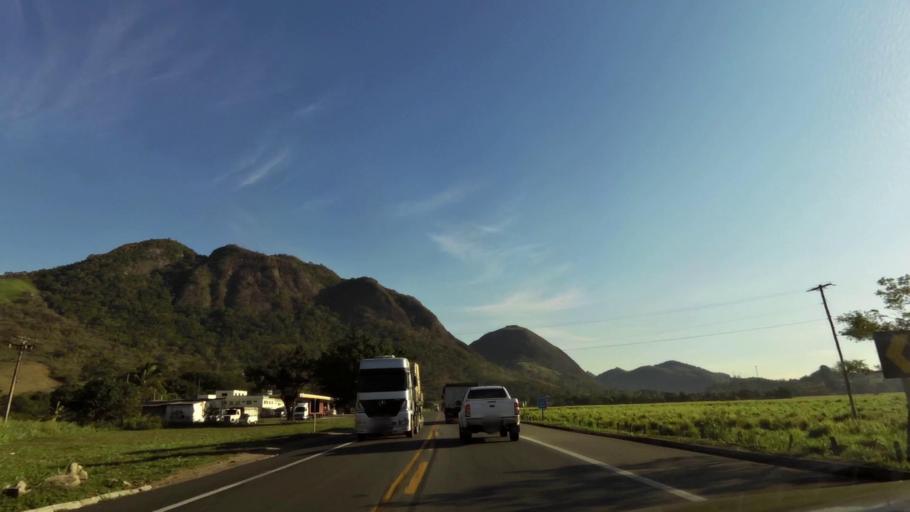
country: BR
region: Espirito Santo
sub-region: Guarapari
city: Guarapari
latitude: -20.6018
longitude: -40.5024
